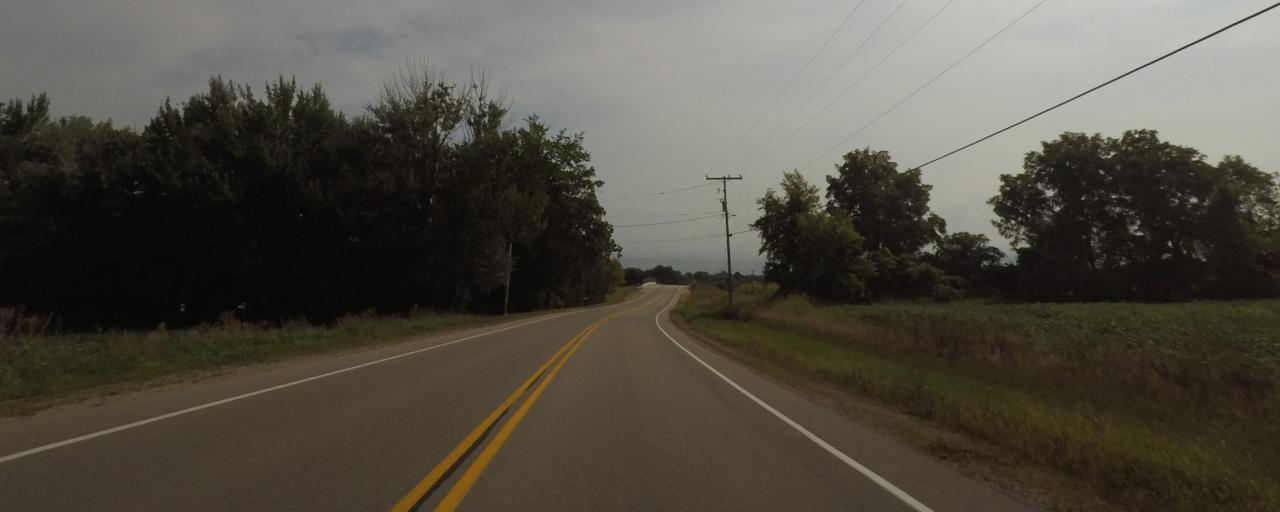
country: US
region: Wisconsin
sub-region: Jefferson County
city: Jefferson
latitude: 42.9934
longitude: -88.8375
